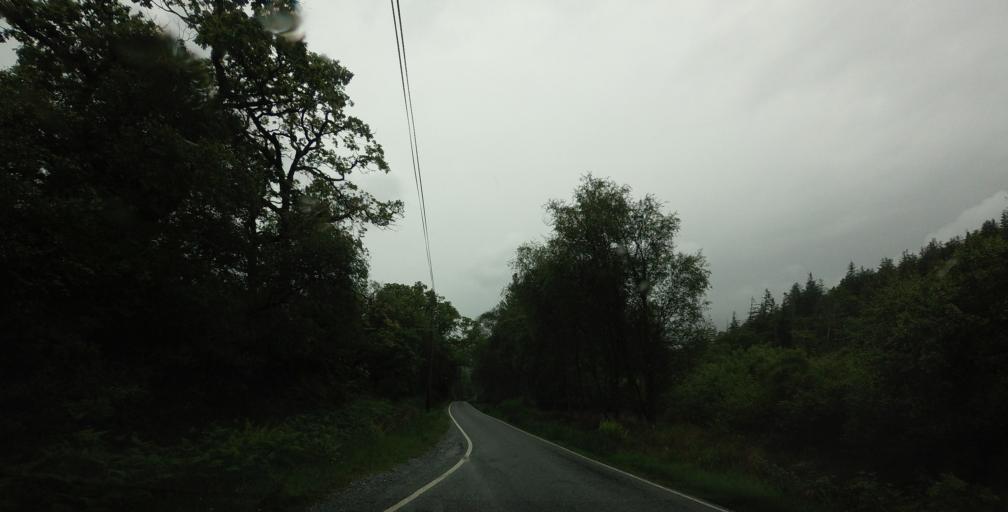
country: GB
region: Scotland
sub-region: Argyll and Bute
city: Isle Of Mull
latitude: 56.7126
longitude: -5.7708
